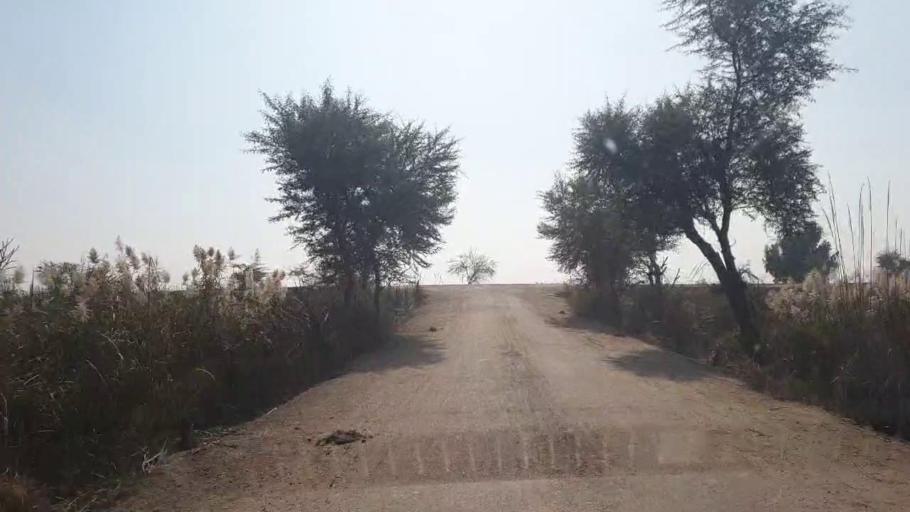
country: PK
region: Sindh
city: Sakrand
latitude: 26.0240
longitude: 68.4385
